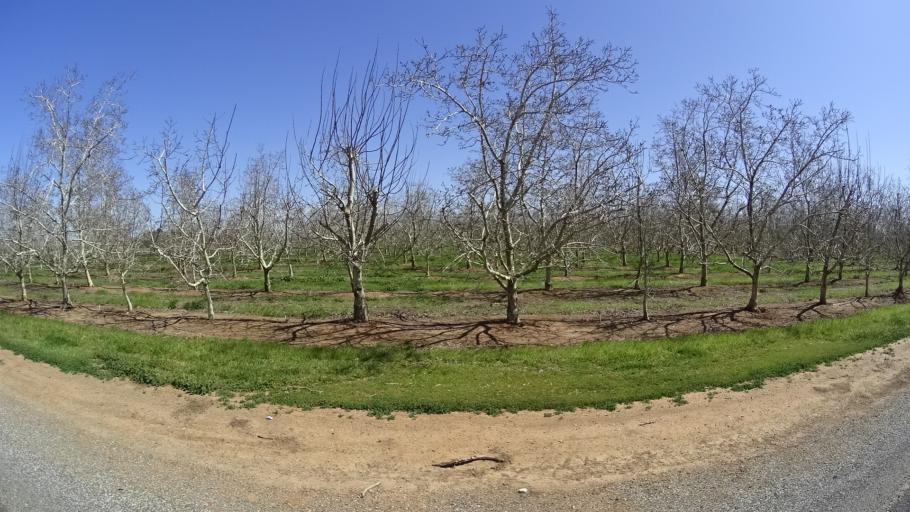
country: US
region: California
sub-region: Glenn County
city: Orland
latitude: 39.7925
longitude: -122.1223
